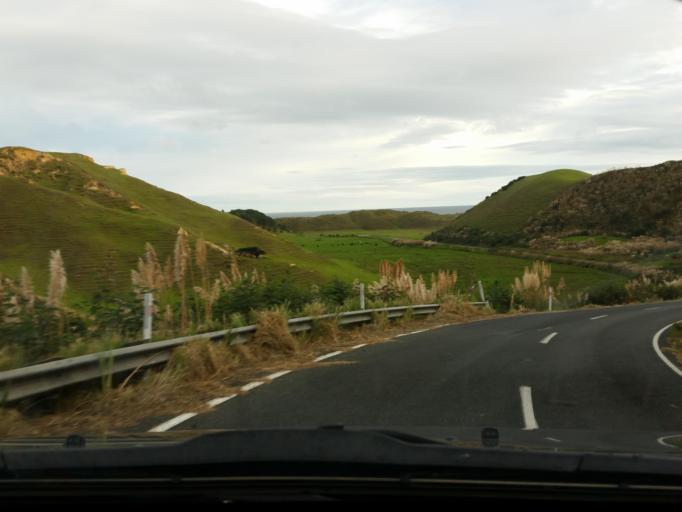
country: NZ
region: Northland
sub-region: Kaipara District
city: Dargaville
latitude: -35.8545
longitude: 173.6683
